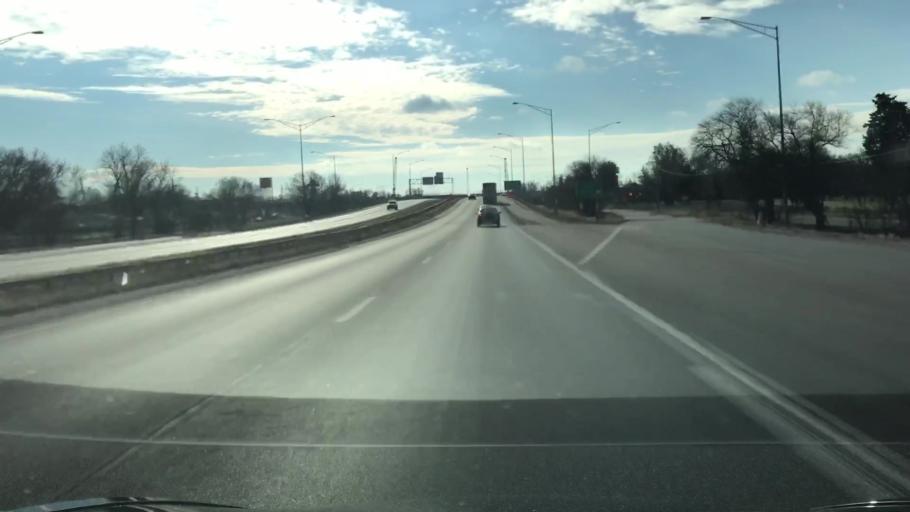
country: US
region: Nebraska
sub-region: Douglas County
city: Omaha
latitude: 41.2570
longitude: -95.9069
